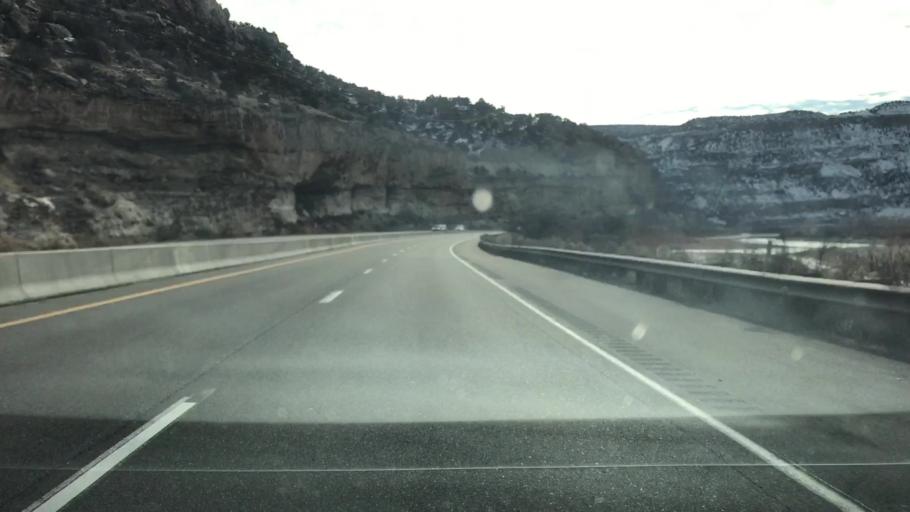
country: US
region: Colorado
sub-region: Mesa County
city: Palisade
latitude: 39.2521
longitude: -108.2585
